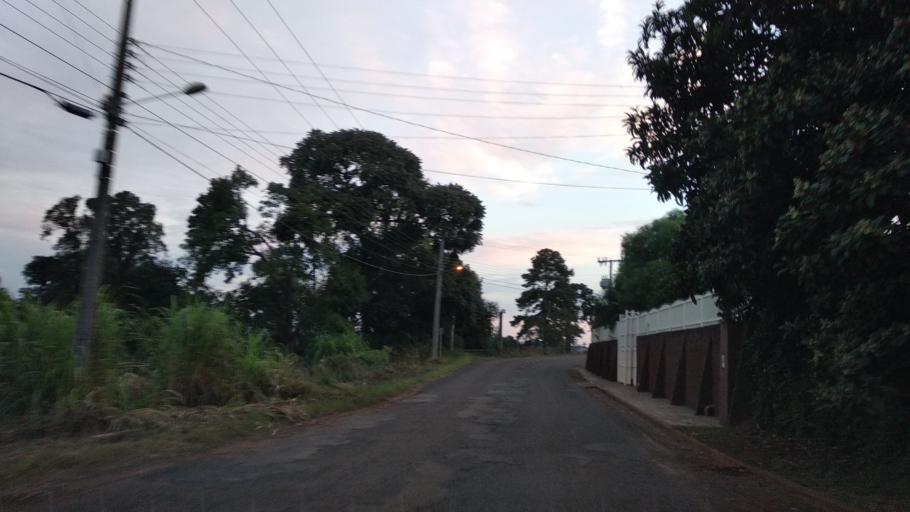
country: BR
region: Santa Catarina
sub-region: Videira
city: Videira
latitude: -26.9960
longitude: -51.1824
